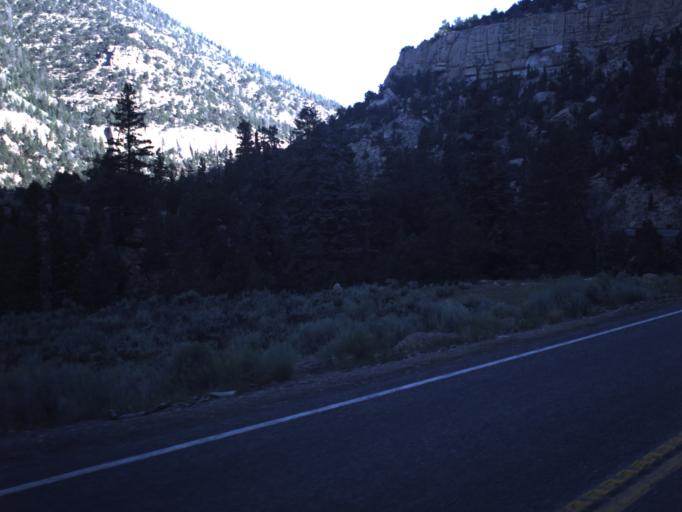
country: US
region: Utah
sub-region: Emery County
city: Huntington
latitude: 39.4224
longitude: -111.1246
